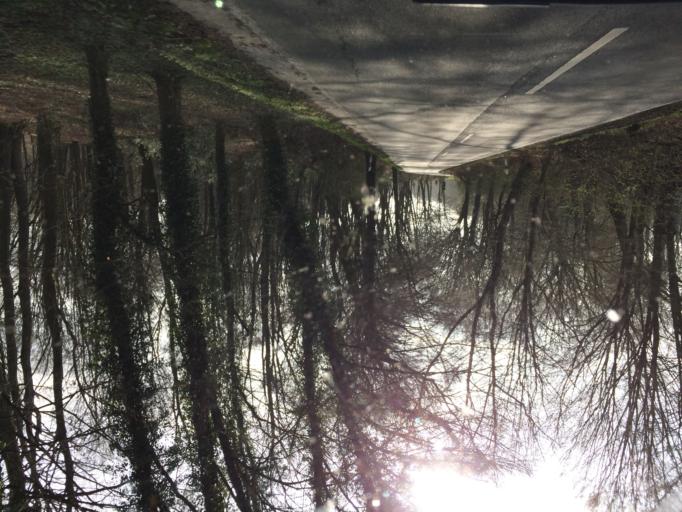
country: DE
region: North Rhine-Westphalia
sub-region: Regierungsbezirk Munster
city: Haltern
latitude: 51.7770
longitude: 7.1253
